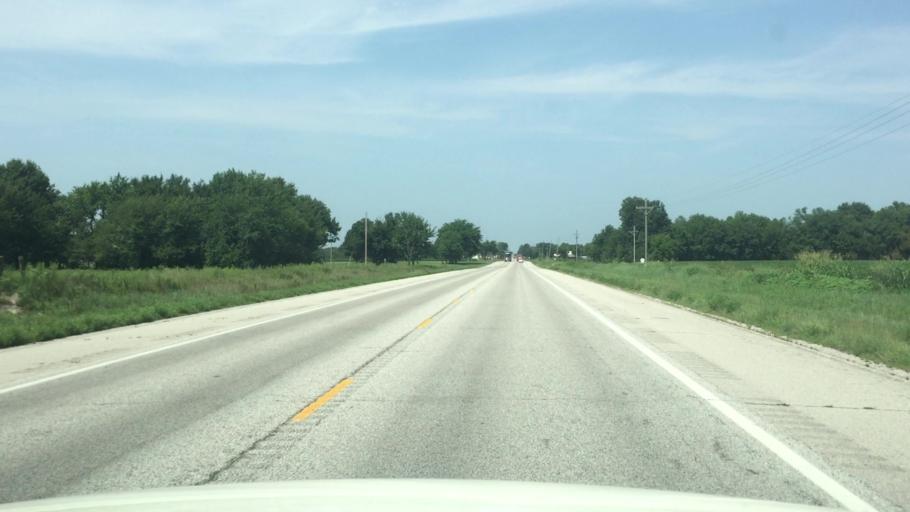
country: US
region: Kansas
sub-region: Cherokee County
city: Galena
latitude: 37.1557
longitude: -94.7043
